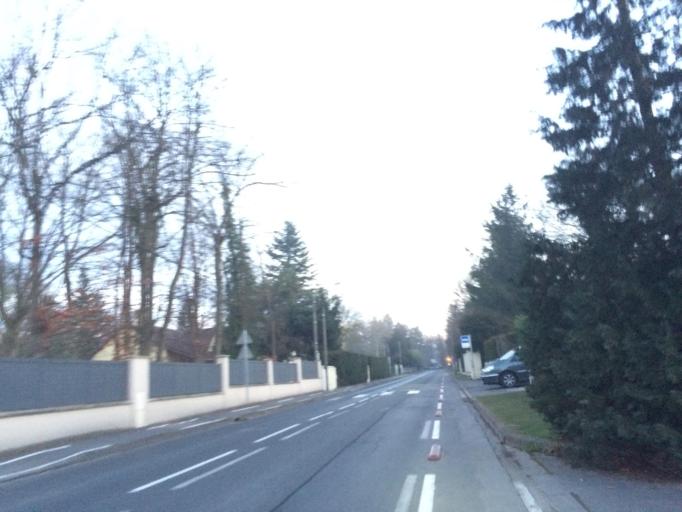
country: FR
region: Picardie
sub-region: Departement de l'Oise
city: Lamorlaye
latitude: 49.1540
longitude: 2.4294
